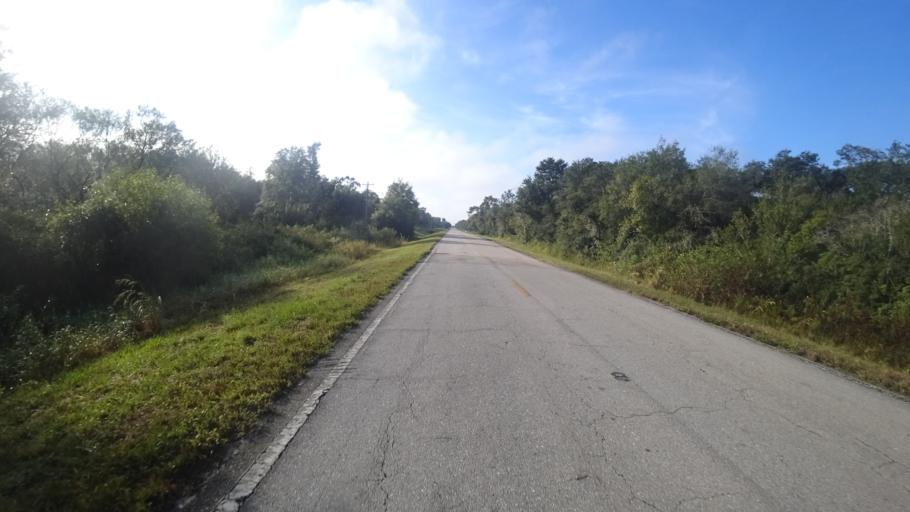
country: US
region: Florida
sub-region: Sarasota County
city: The Meadows
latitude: 27.4142
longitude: -82.3037
